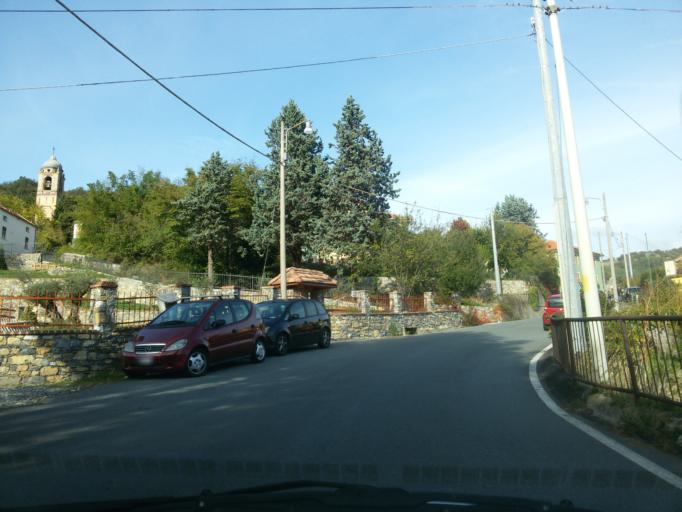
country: IT
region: Liguria
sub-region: Provincia di Genova
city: Piccarello
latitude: 44.4660
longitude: 8.9622
